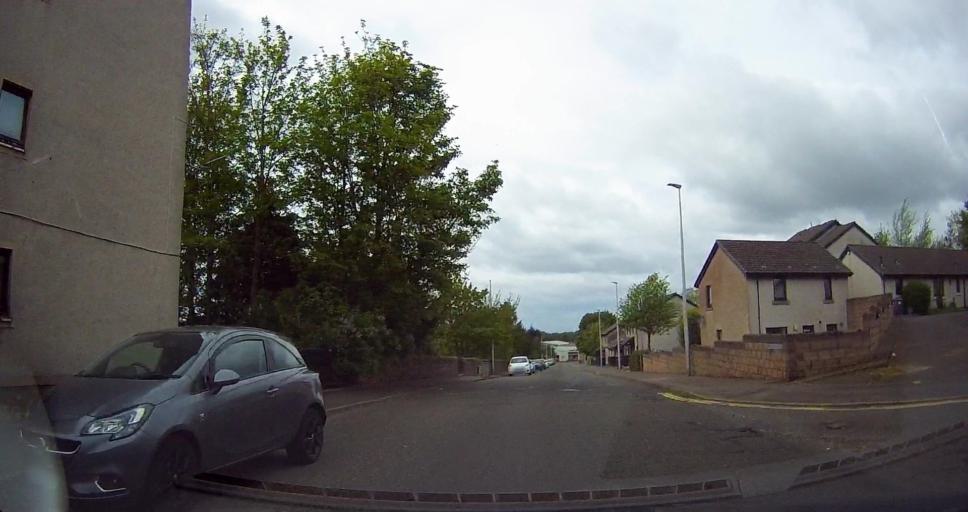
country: GB
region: Scotland
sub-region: Angus
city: Forfar
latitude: 56.6480
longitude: -2.8838
